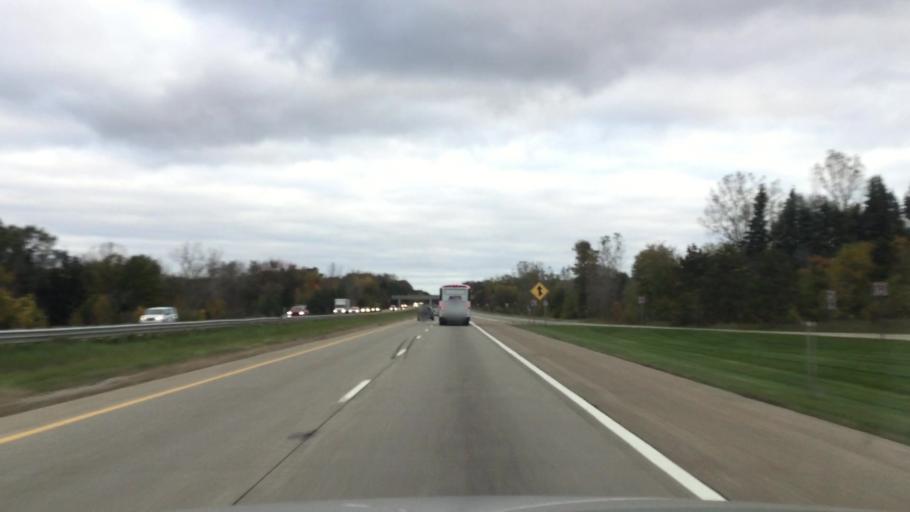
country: US
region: Michigan
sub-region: Genesee County
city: Lake Fenton
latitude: 42.8364
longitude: -83.7341
